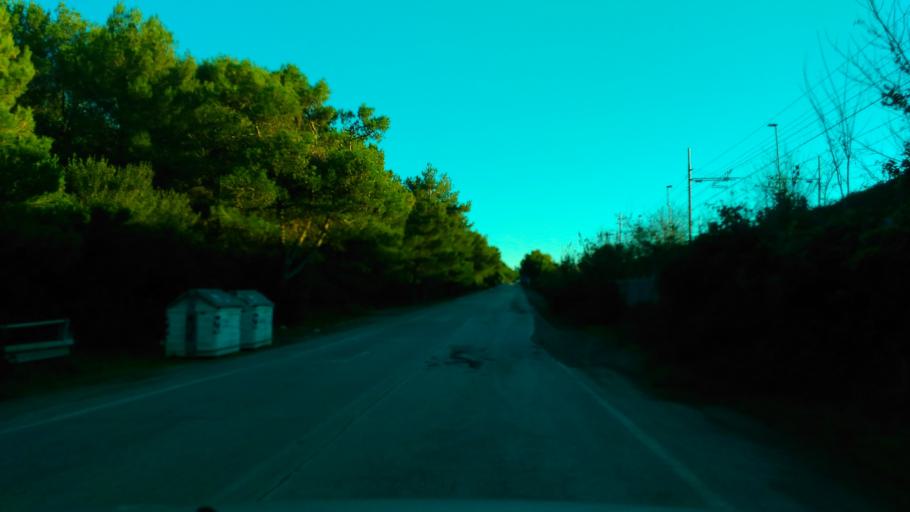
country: IT
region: Tuscany
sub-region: Provincia di Livorno
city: Quercianella
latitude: 43.4492
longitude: 10.3798
